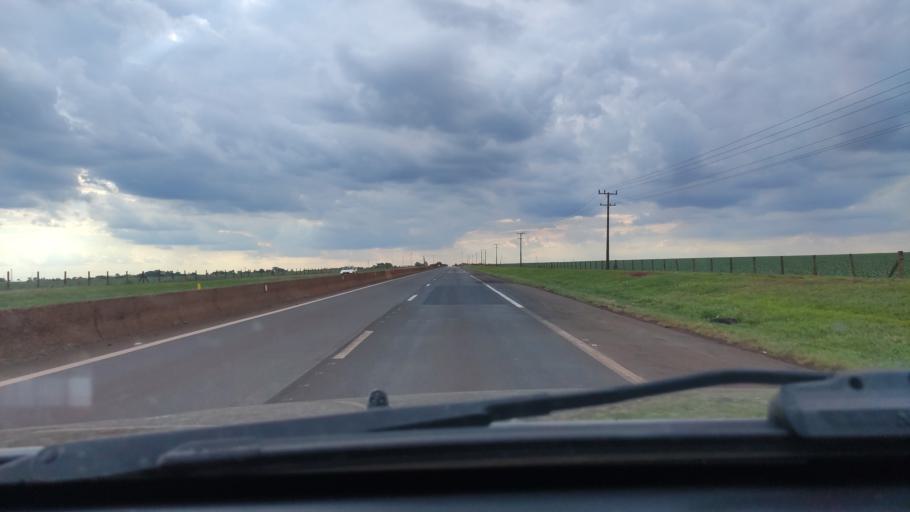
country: BR
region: Sao Paulo
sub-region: Palmital
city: Palmital
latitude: -22.8206
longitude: -50.0437
